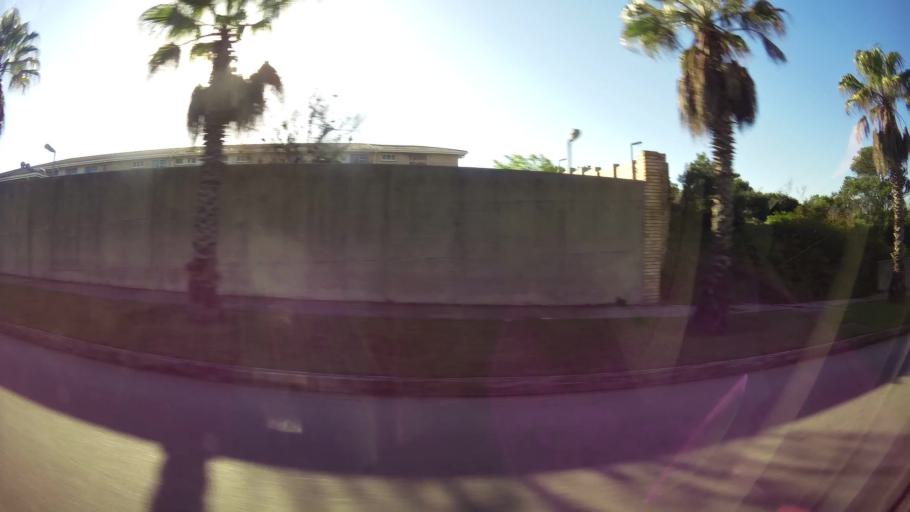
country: ZA
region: Eastern Cape
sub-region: Nelson Mandela Bay Metropolitan Municipality
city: Port Elizabeth
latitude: -33.9751
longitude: 25.6258
